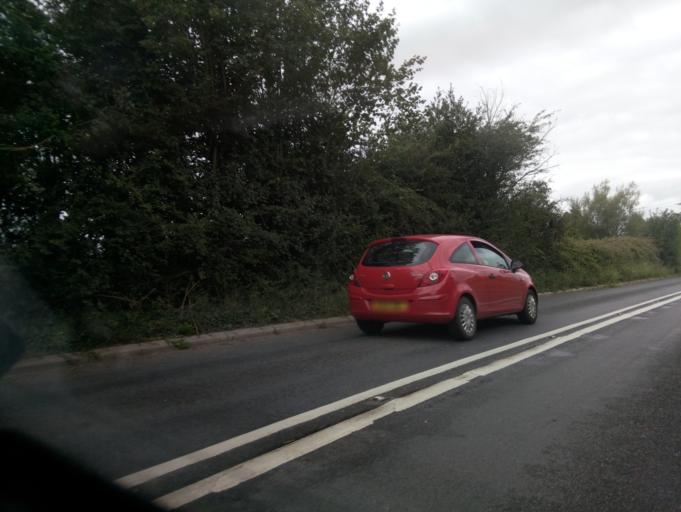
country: GB
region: England
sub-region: Devon
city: Cullompton
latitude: 50.8757
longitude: -3.3869
